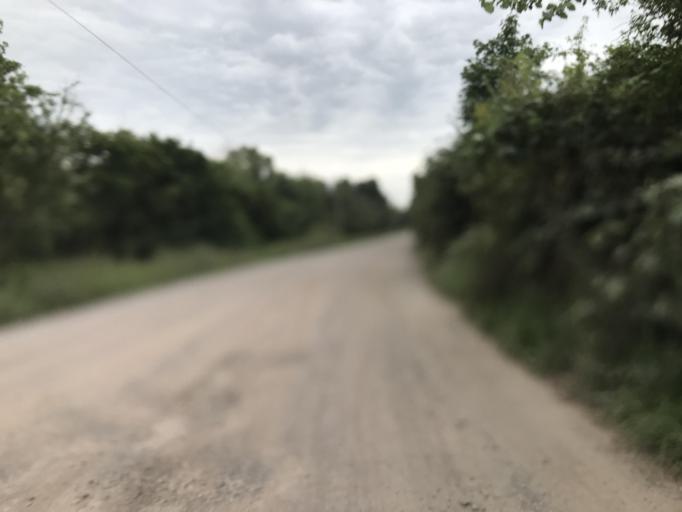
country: DE
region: Saxony-Anhalt
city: Quedlinburg
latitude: 51.7769
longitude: 11.1274
